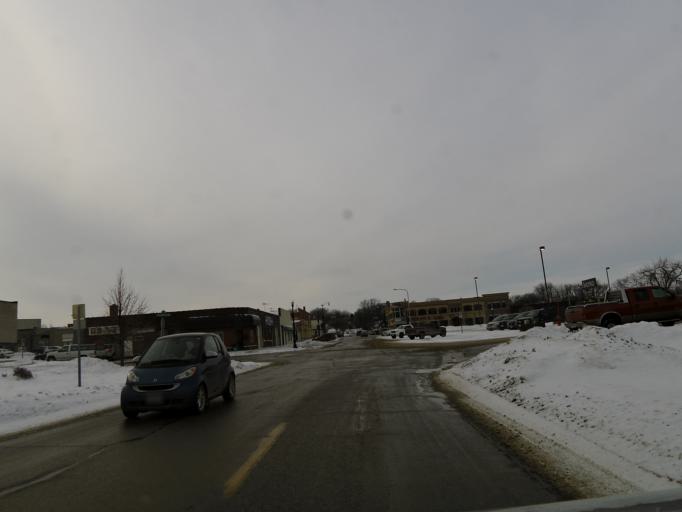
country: US
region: Minnesota
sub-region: McLeod County
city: Hutchinson
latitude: 44.8934
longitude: -94.3674
